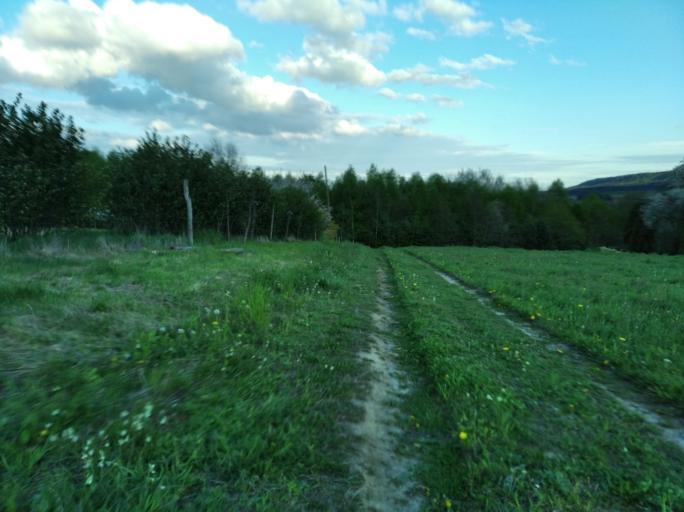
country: PL
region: Subcarpathian Voivodeship
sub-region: Powiat strzyzowski
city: Strzyzow
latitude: 49.8538
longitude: 21.7653
